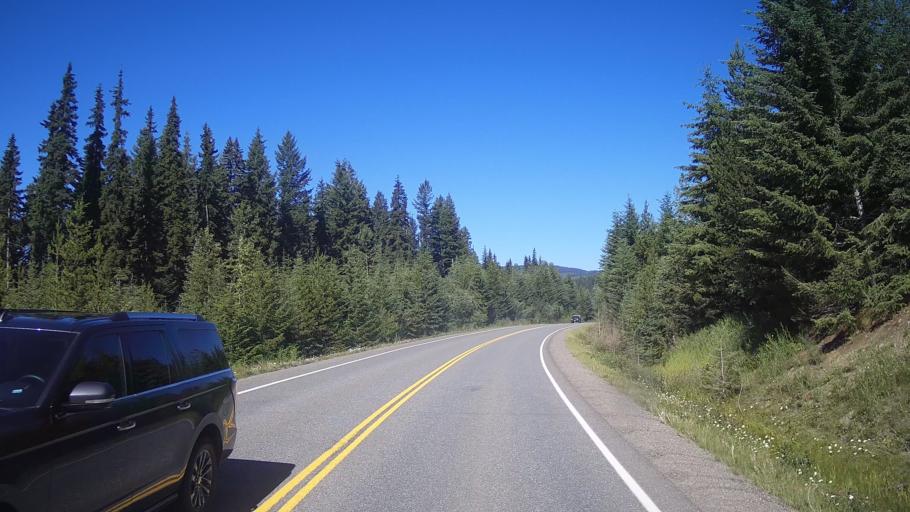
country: CA
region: British Columbia
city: Kamloops
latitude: 51.4969
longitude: -120.4309
